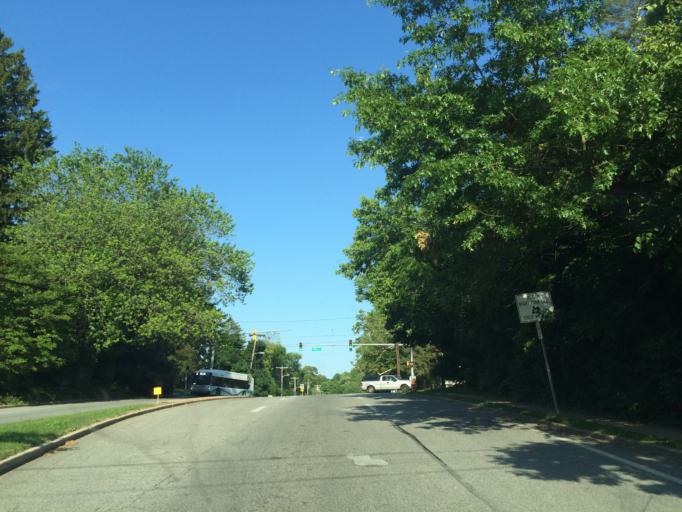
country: US
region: Maryland
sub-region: Howard County
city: Ilchester
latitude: 39.2738
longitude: -76.7573
